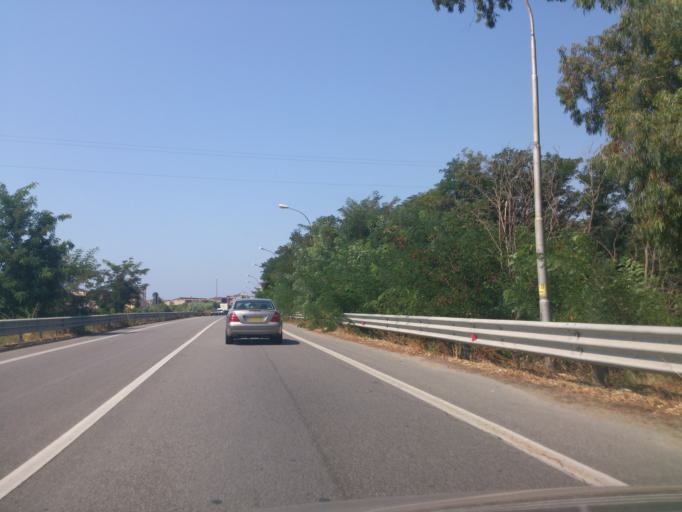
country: IT
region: Calabria
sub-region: Provincia di Reggio Calabria
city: Caulonia Marina
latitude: 38.3473
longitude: 16.4718
